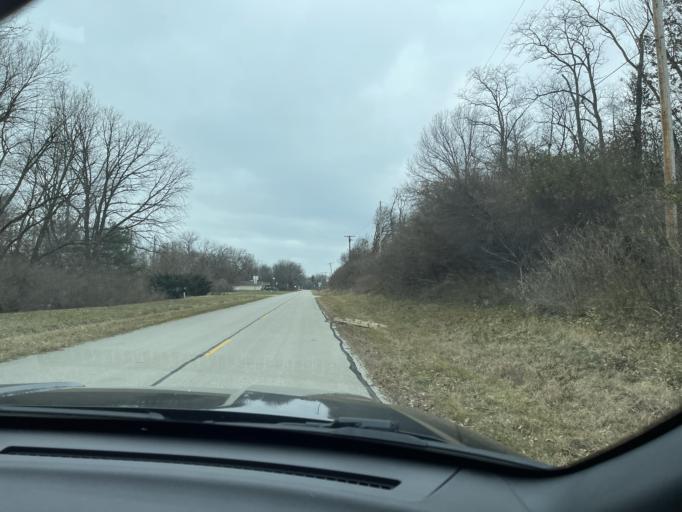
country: US
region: Illinois
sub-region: Sangamon County
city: Grandview
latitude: 39.7997
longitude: -89.6002
